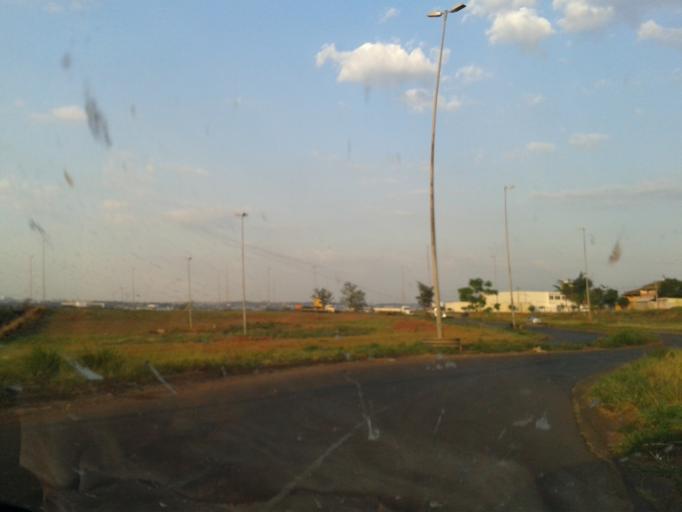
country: BR
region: Minas Gerais
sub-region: Uberlandia
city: Uberlandia
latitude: -18.9078
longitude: -48.3318
